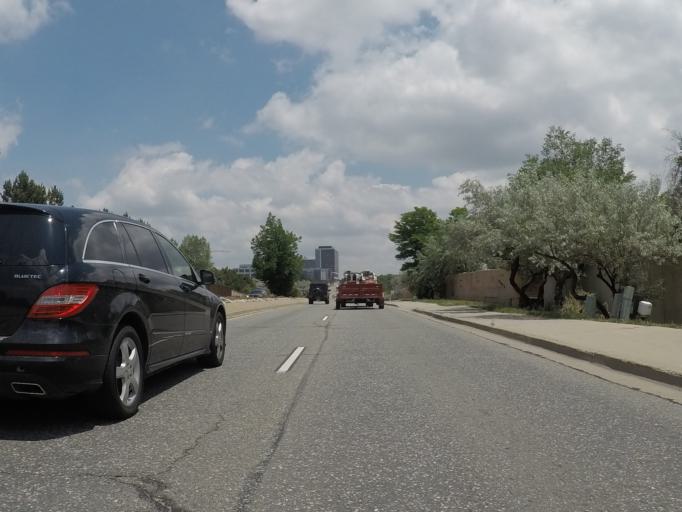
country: US
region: Colorado
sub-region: Arapahoe County
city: Greenwood Village
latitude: 39.6240
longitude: -104.9185
